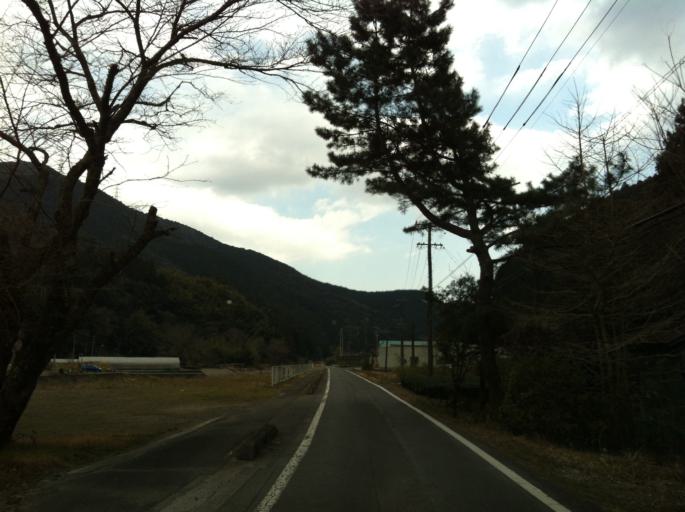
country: JP
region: Shizuoka
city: Shizuoka-shi
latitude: 35.0641
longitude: 138.3340
